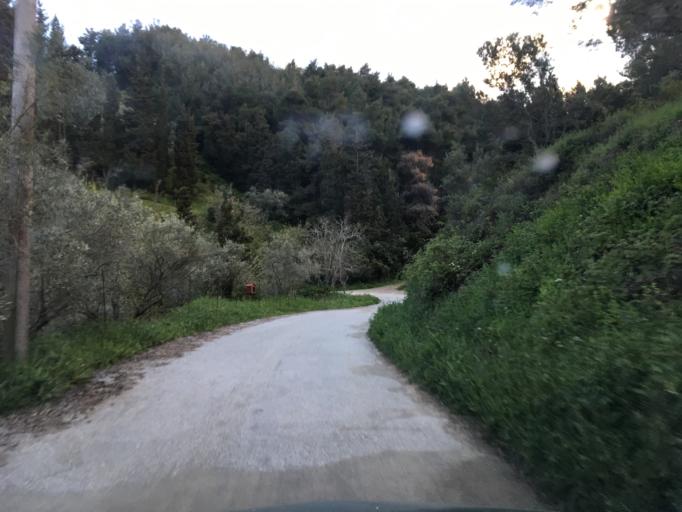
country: GR
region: Thessaly
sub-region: Nomos Magnisias
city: Skopelos
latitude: 39.1815
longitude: 23.6190
